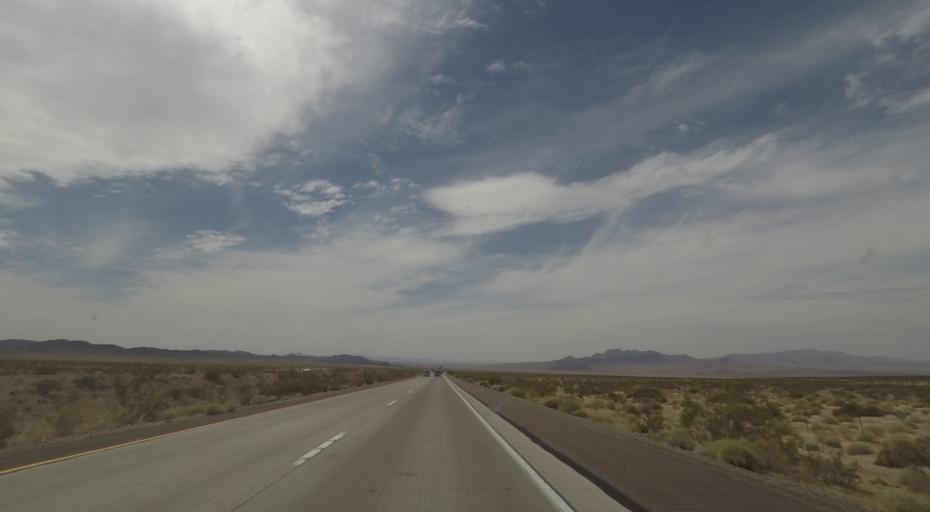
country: US
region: California
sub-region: San Bernardino County
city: Twentynine Palms
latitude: 34.7277
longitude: -116.0873
